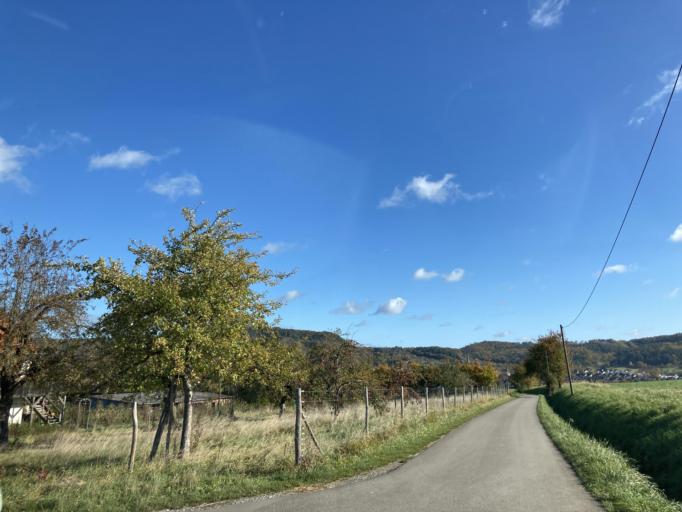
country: DE
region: Baden-Wuerttemberg
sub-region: Regierungsbezirk Stuttgart
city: Hildrizhausen
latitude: 48.5523
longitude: 8.9527
